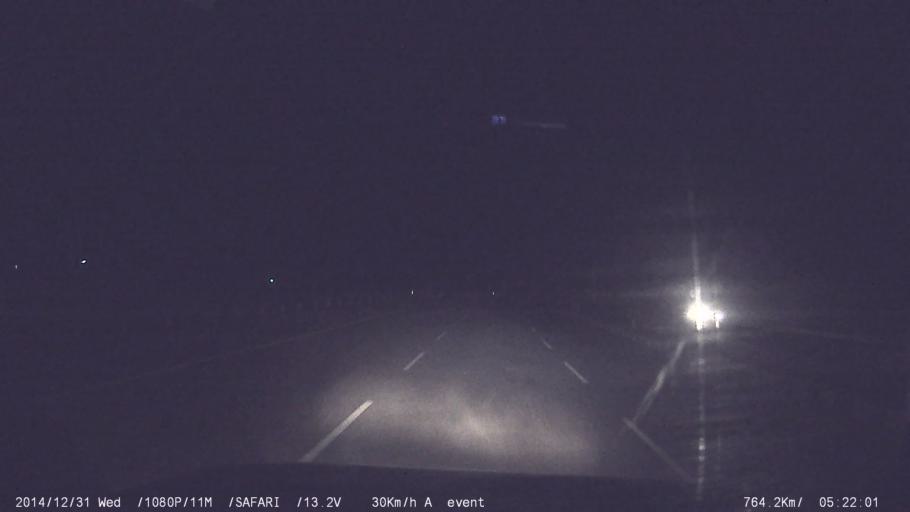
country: IN
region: Tamil Nadu
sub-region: Cuddalore
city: Vriddhachalam
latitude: 11.6968
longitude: 79.2666
